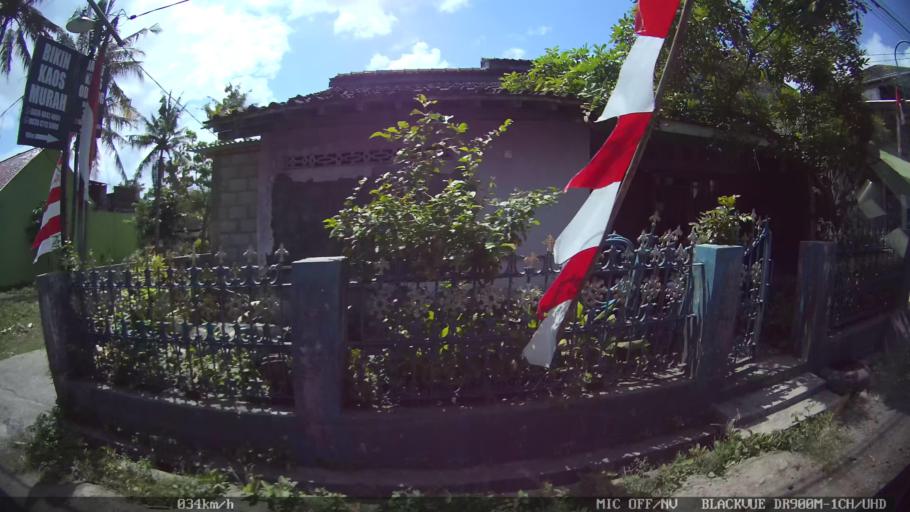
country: ID
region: Daerah Istimewa Yogyakarta
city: Sewon
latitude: -7.8718
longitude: 110.3643
